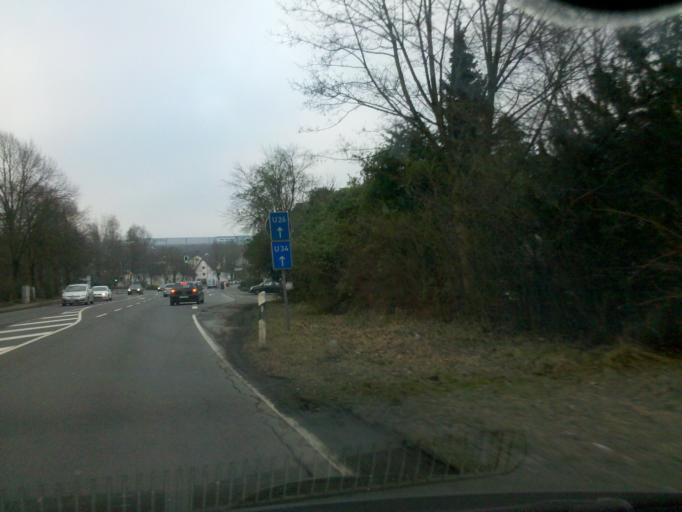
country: DE
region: North Rhine-Westphalia
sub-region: Regierungsbezirk Arnsberg
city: Olpe
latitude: 51.0049
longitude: 7.8413
